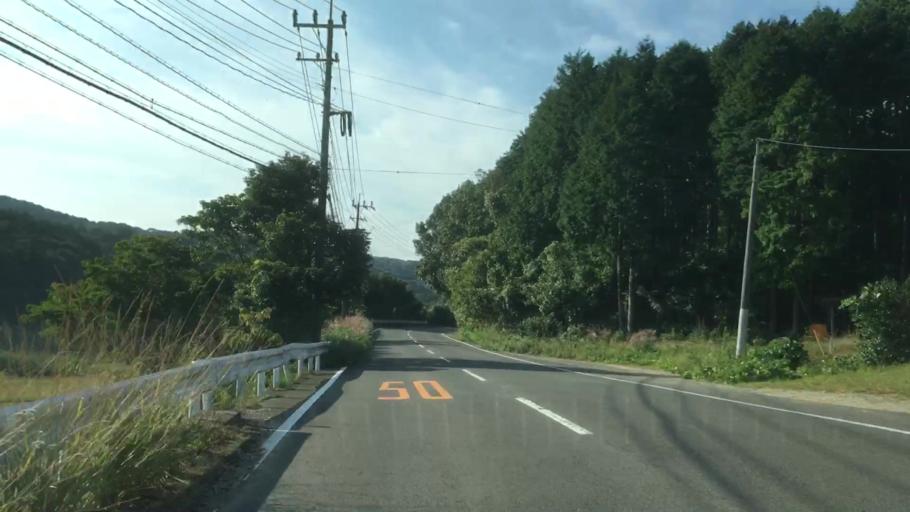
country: JP
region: Nagasaki
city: Sasebo
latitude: 32.9552
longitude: 129.6754
